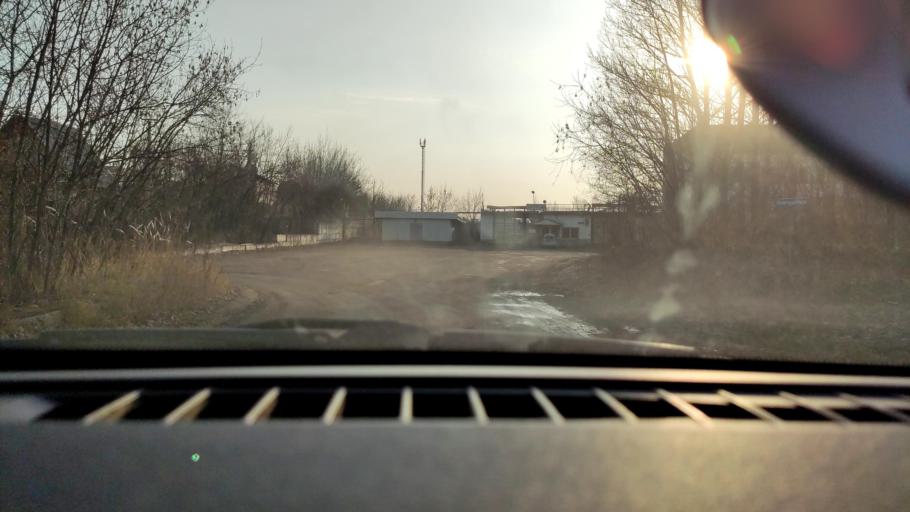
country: RU
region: Perm
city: Kondratovo
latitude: 57.9573
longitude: 56.1523
